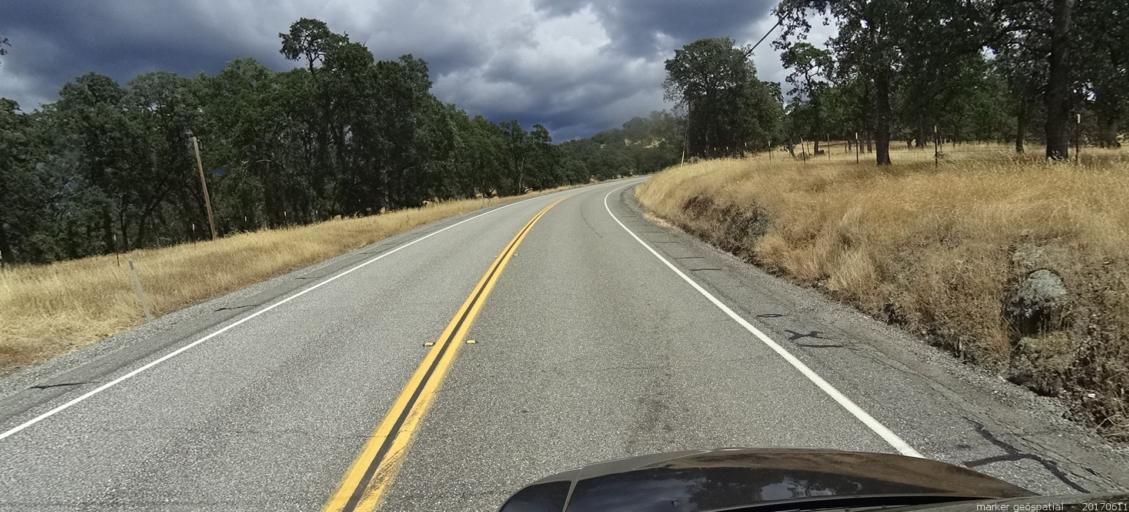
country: US
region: California
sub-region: Butte County
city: Paradise
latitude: 39.6570
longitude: -121.5749
